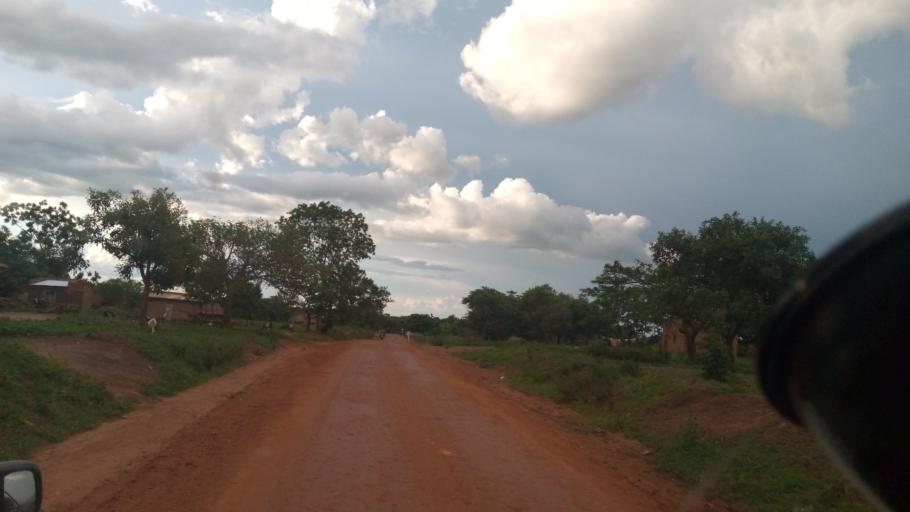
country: UG
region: Northern Region
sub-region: Lira District
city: Lira
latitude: 2.3780
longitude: 32.9331
